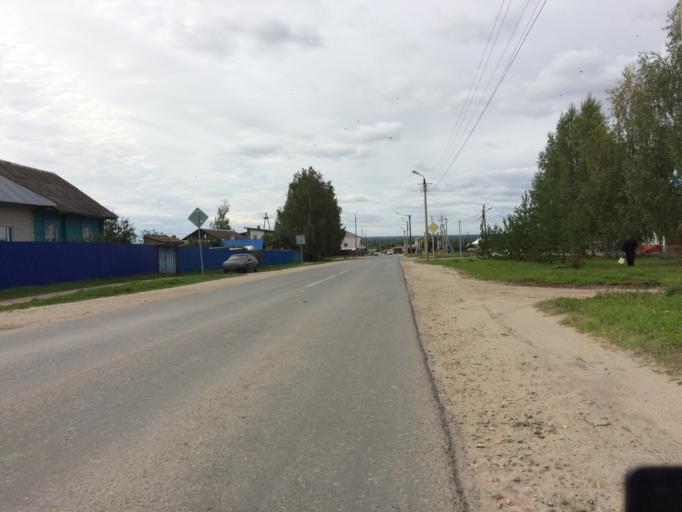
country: RU
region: Mariy-El
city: Yoshkar-Ola
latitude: 56.6565
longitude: 47.9746
